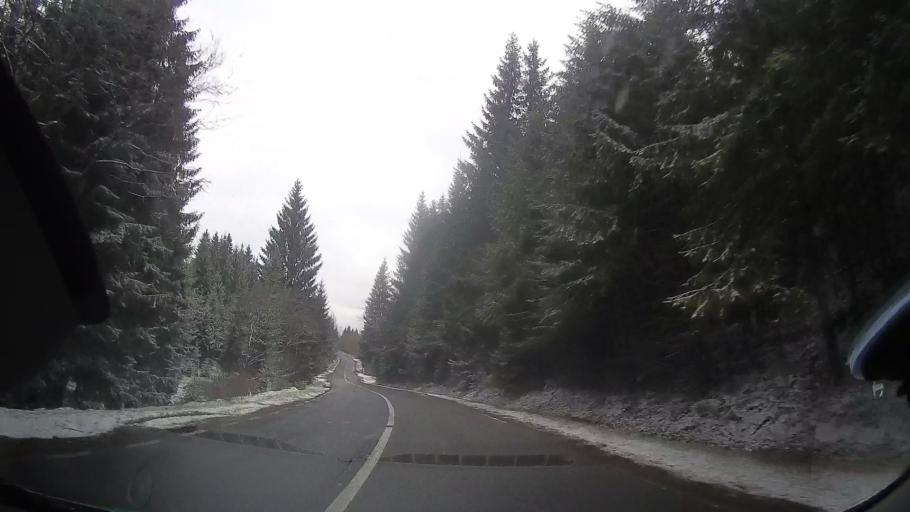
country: RO
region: Cluj
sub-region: Comuna Calatele
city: Calatele
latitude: 46.7198
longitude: 23.0434
